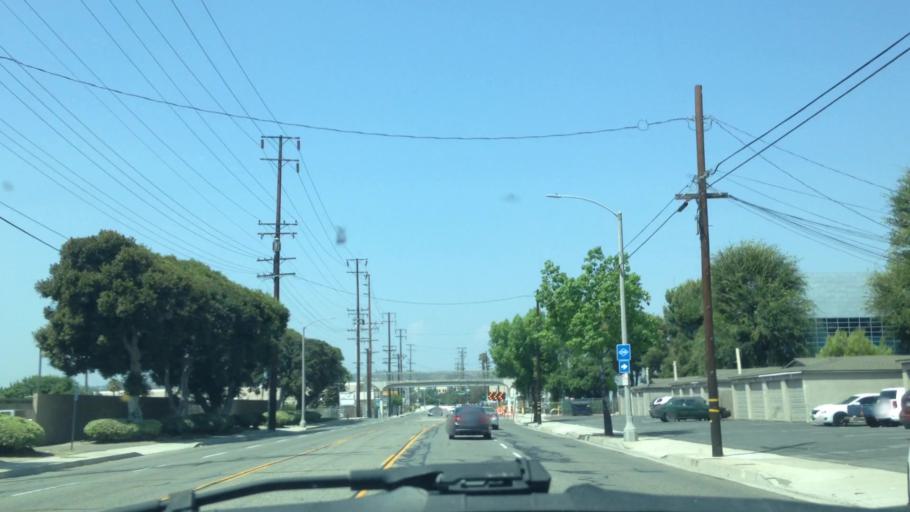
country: US
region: California
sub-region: Orange County
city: Fullerton
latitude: 33.8673
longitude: -117.9594
